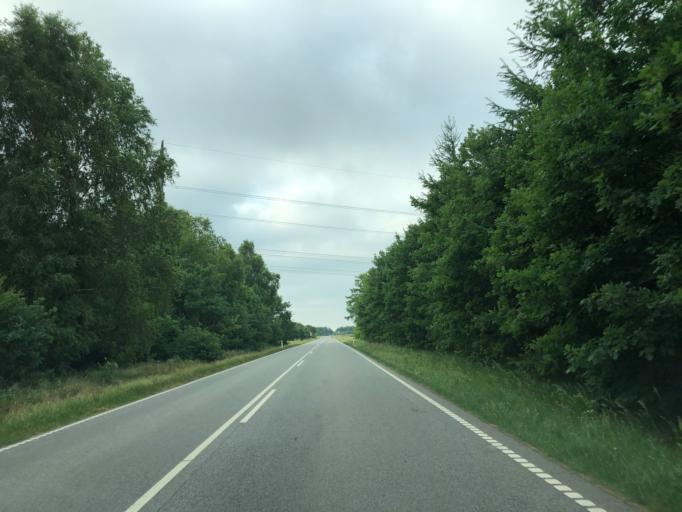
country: DK
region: Central Jutland
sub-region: Ikast-Brande Kommune
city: Brande
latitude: 55.9176
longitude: 9.1708
